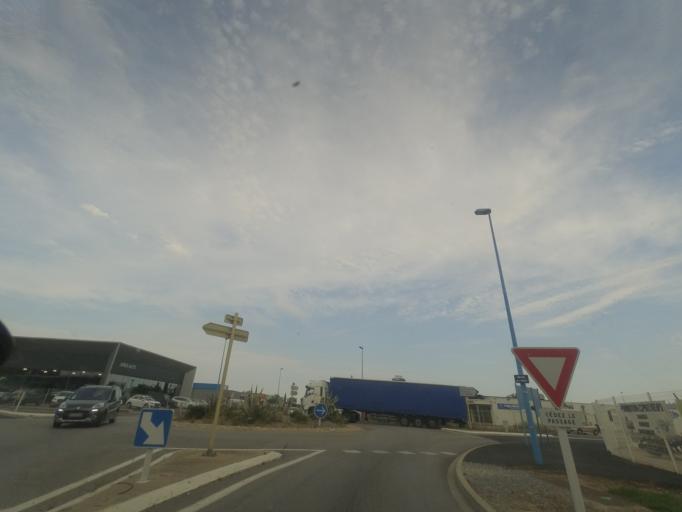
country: FR
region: Languedoc-Roussillon
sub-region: Departement des Pyrenees-Orientales
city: Baho
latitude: 42.6875
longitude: 2.8222
